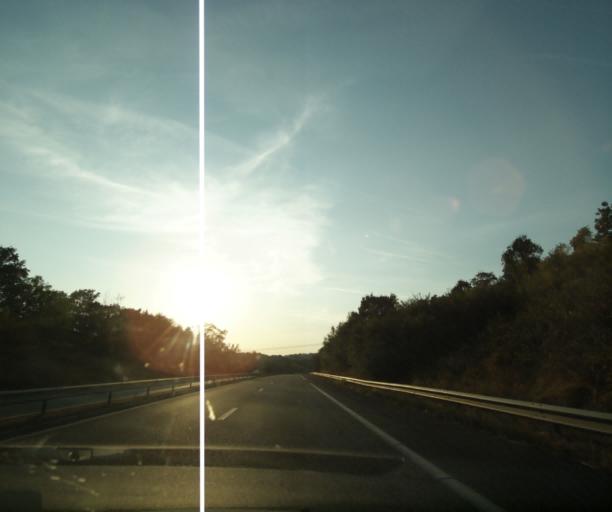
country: FR
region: Midi-Pyrenees
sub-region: Departement du Tarn-et-Garonne
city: Lamagistere
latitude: 44.0702
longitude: 0.8201
